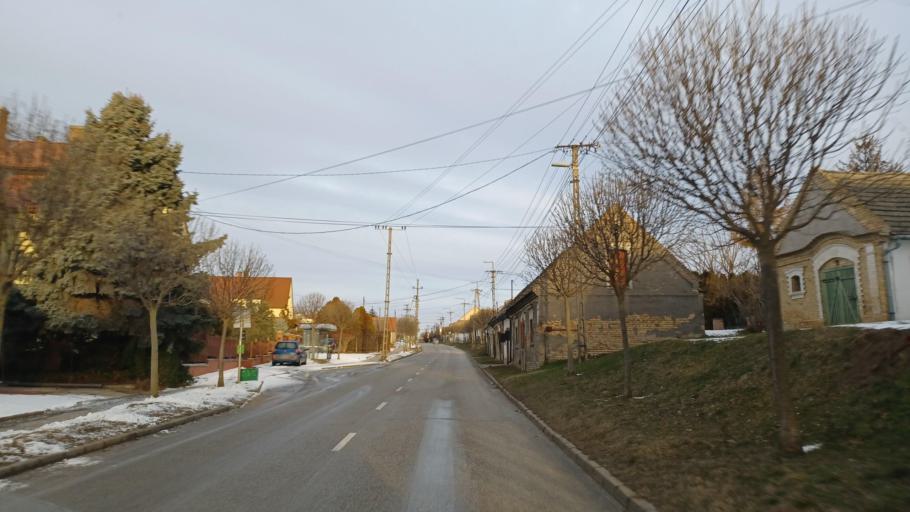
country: HU
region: Tolna
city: Paks
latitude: 46.6288
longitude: 18.8564
